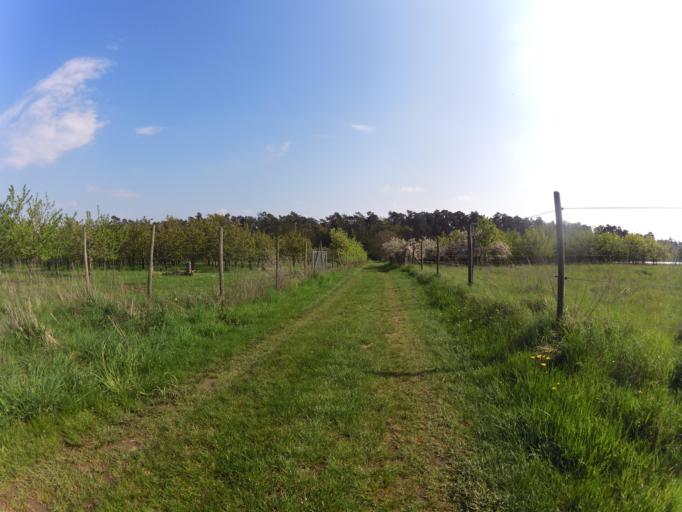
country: DE
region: Bavaria
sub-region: Regierungsbezirk Unterfranken
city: Sommerhausen
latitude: 49.7077
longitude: 10.0477
